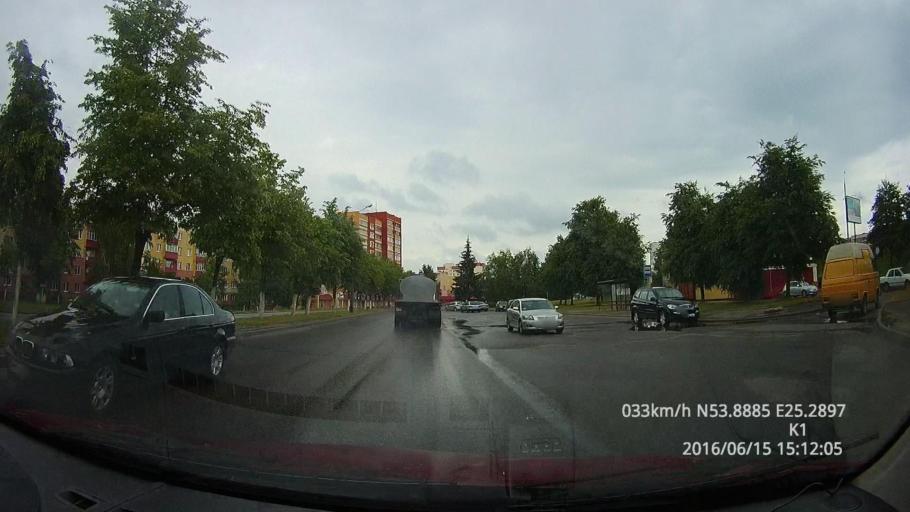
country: BY
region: Grodnenskaya
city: Lida
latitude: 53.8886
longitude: 25.2900
